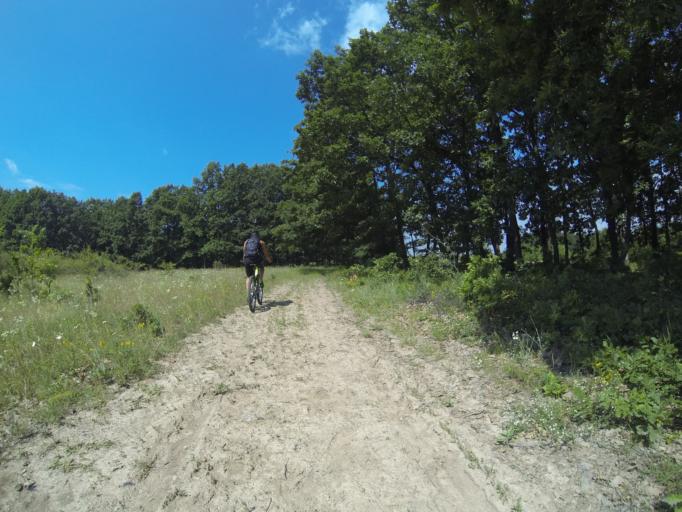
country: RO
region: Gorj
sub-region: Comuna Crusetu
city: Crusetu
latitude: 44.6146
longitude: 23.6281
